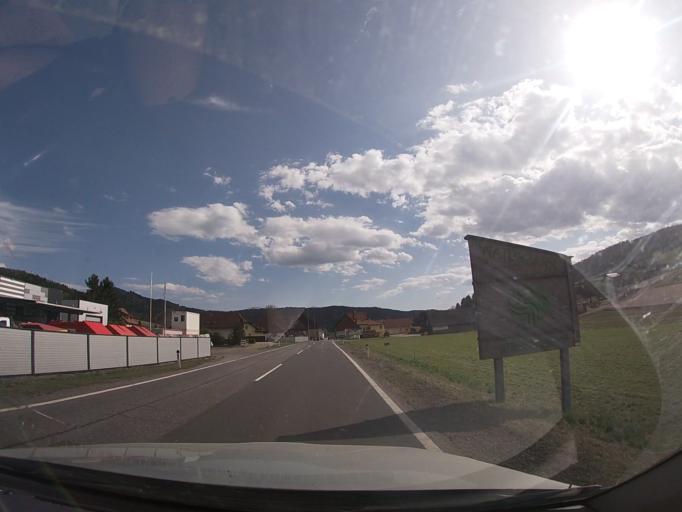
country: AT
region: Styria
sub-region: Politischer Bezirk Murau
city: Perchau am Sattel
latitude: 47.1100
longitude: 14.4577
